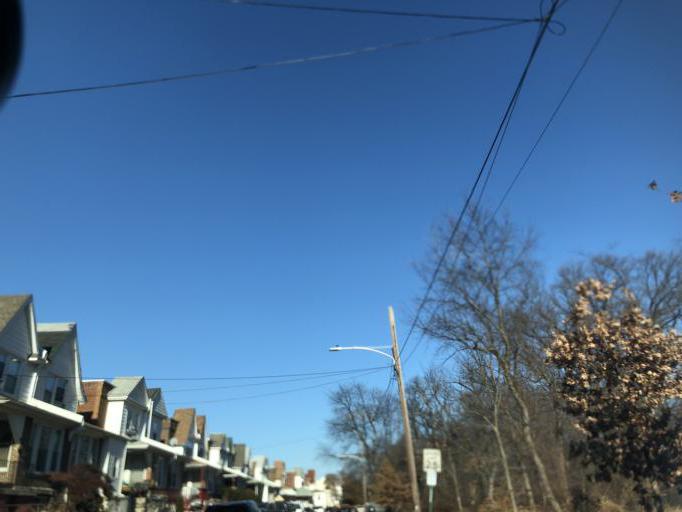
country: US
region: Pennsylvania
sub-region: Delaware County
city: Millbourne
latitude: 39.9573
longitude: -75.2516
